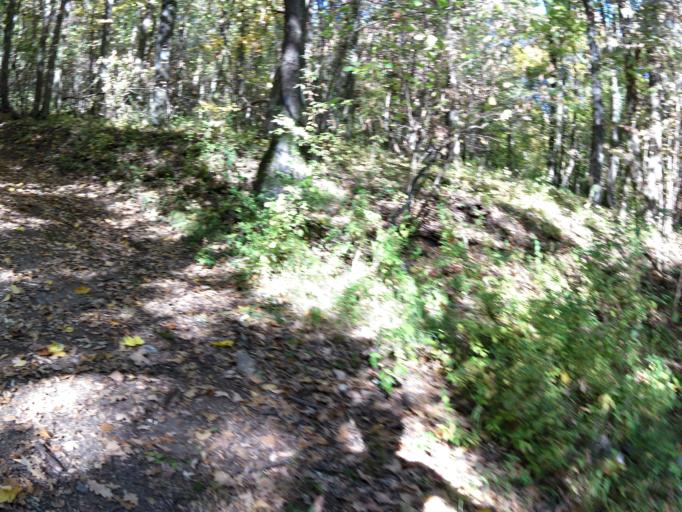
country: DE
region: Bavaria
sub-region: Regierungsbezirk Unterfranken
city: Eibelstadt
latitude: 49.7226
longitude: 9.9836
